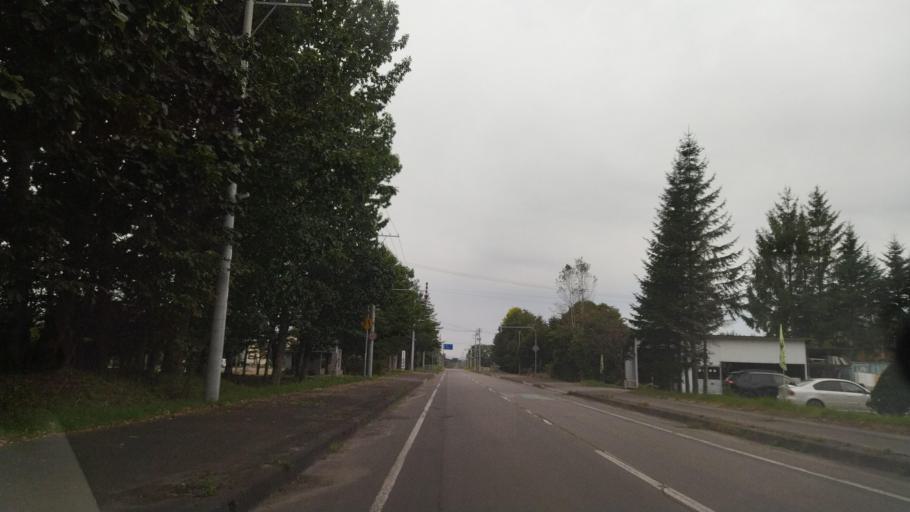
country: JP
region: Hokkaido
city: Otofuke
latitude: 43.2296
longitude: 143.2788
